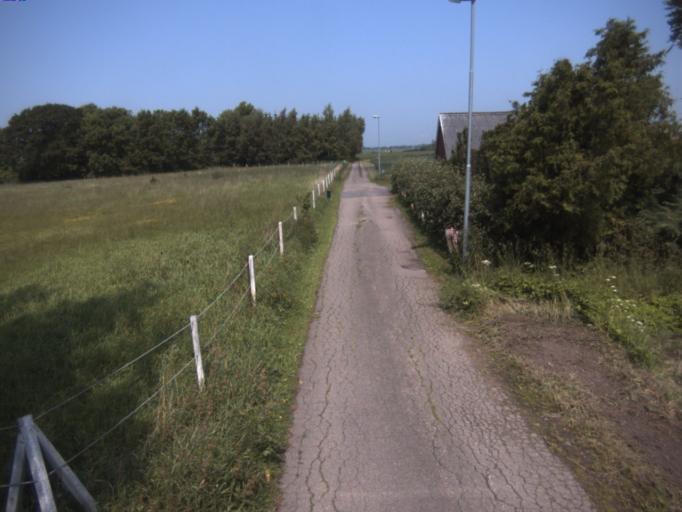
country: SE
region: Skane
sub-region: Angelholms Kommun
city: Strovelstorp
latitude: 56.1456
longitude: 12.7677
